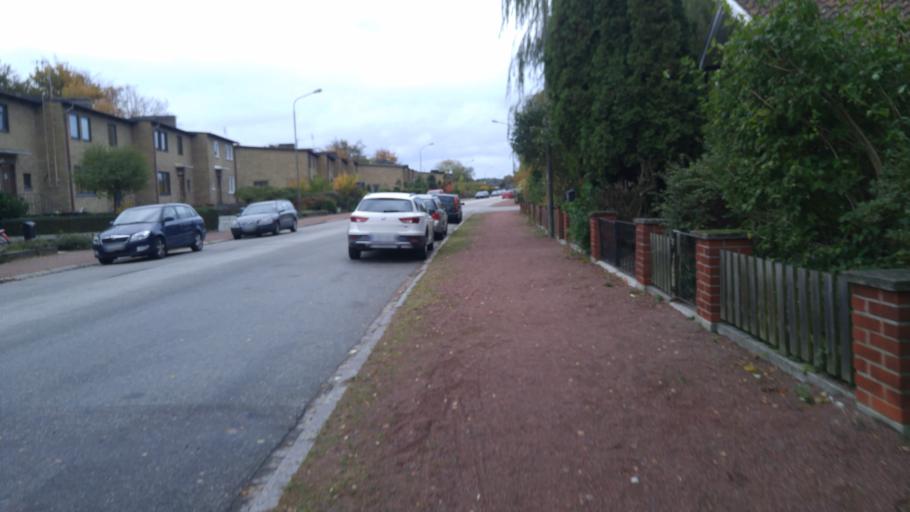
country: SE
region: Skane
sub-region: Malmo
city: Bunkeflostrand
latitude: 55.5776
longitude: 12.9520
